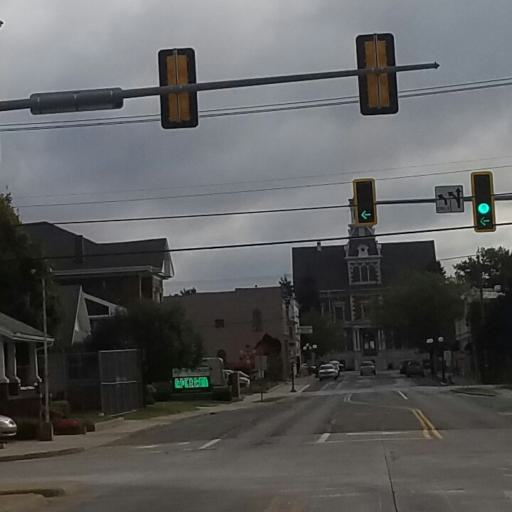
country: US
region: Illinois
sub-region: McDonough County
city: Macomb
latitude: 40.4587
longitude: -90.6753
